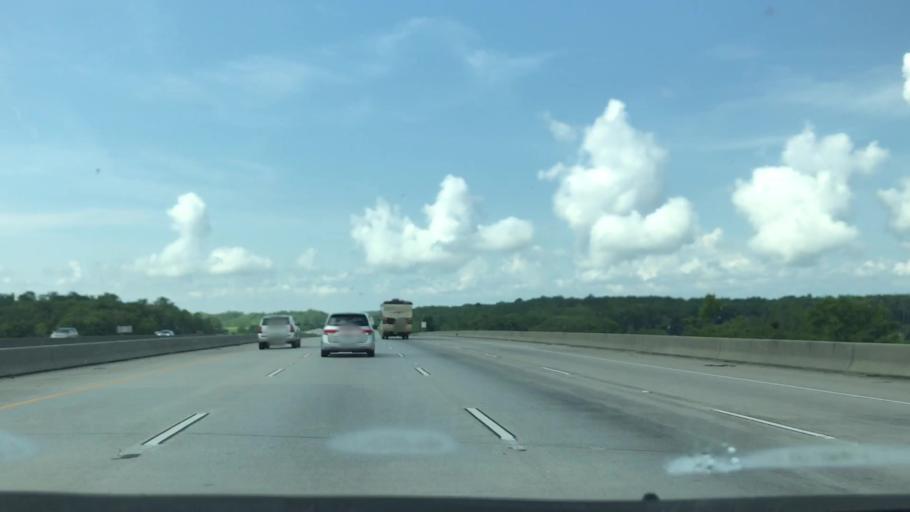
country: US
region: Georgia
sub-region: McIntosh County
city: Darien
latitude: 31.3361
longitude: -81.4674
